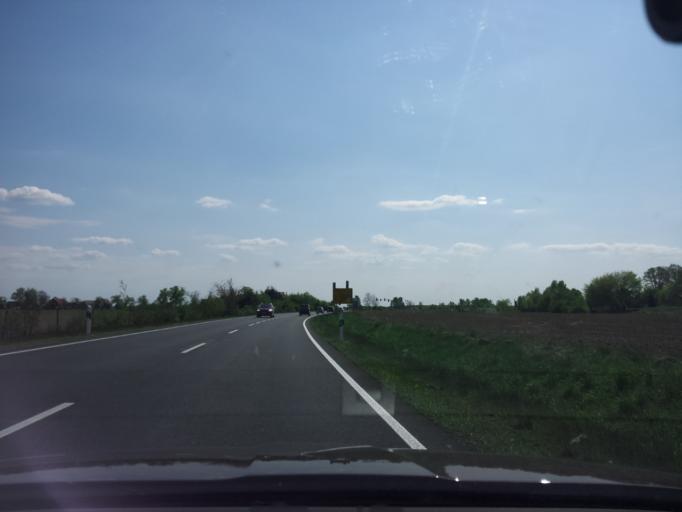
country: DE
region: Brandenburg
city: Beelitz
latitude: 52.2371
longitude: 12.9879
